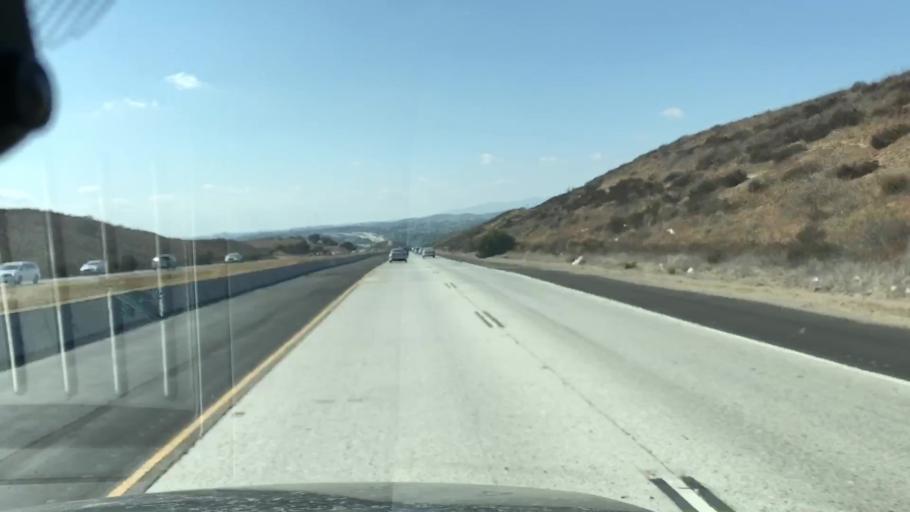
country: US
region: California
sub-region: Ventura County
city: Simi Valley
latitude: 34.2918
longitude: -118.8225
